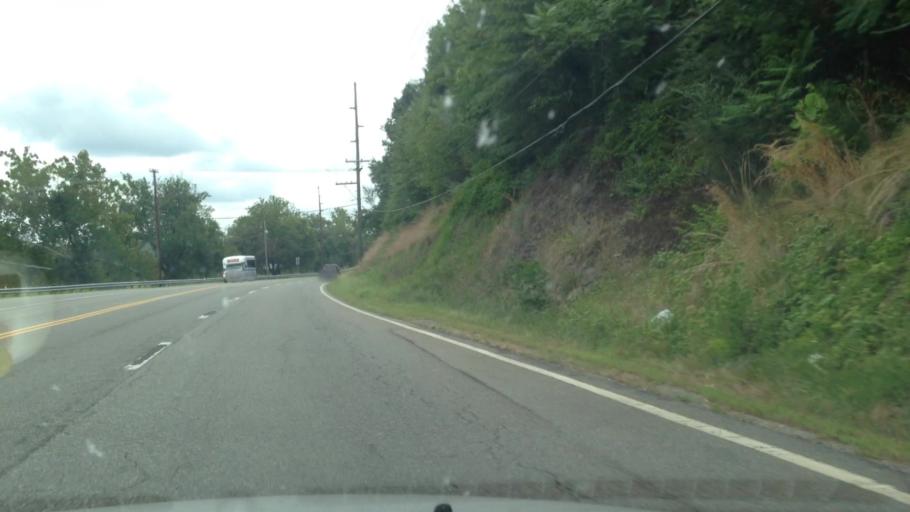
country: US
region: Virginia
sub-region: City of Danville
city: Danville
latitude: 36.5852
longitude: -79.4181
